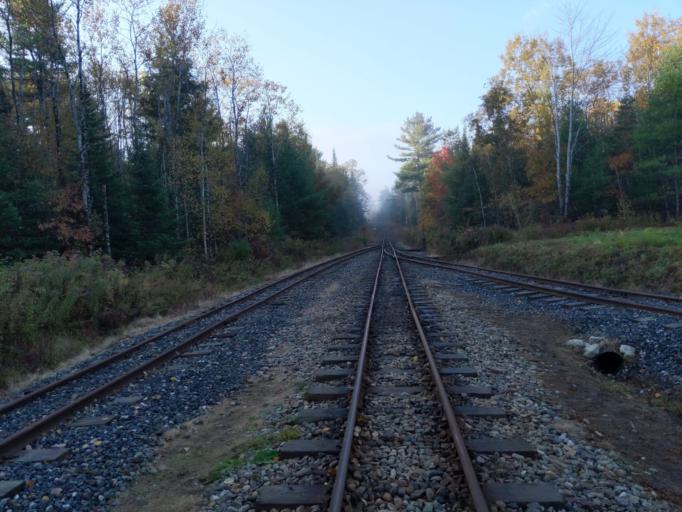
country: US
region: Maine
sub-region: Lincoln County
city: Whitefield
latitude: 44.0952
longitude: -69.6243
